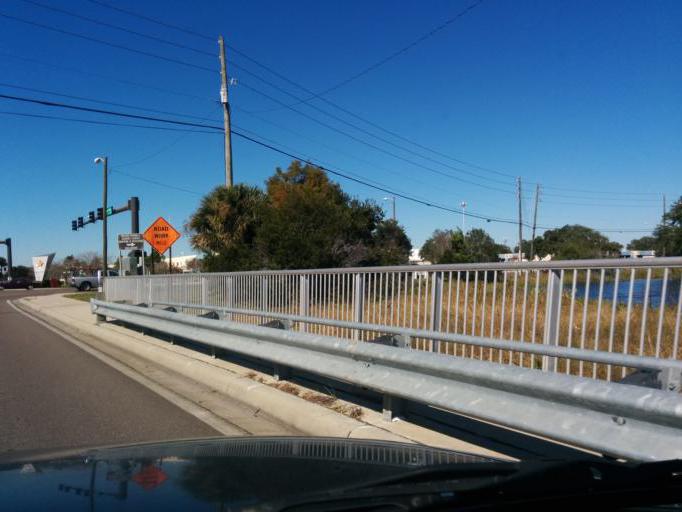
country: US
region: Florida
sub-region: Pinellas County
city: Pinellas Park
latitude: 27.8725
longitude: -82.7448
